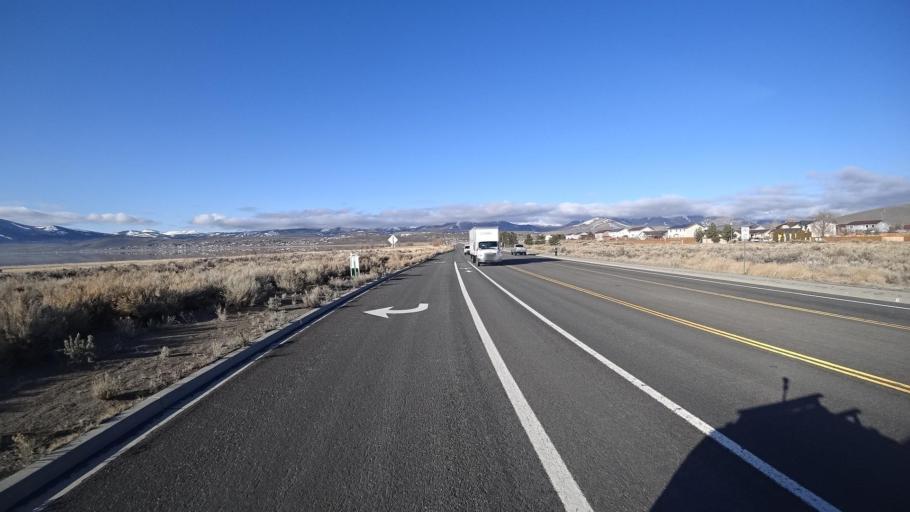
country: US
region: Nevada
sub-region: Washoe County
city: Cold Springs
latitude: 39.6755
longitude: -119.9797
